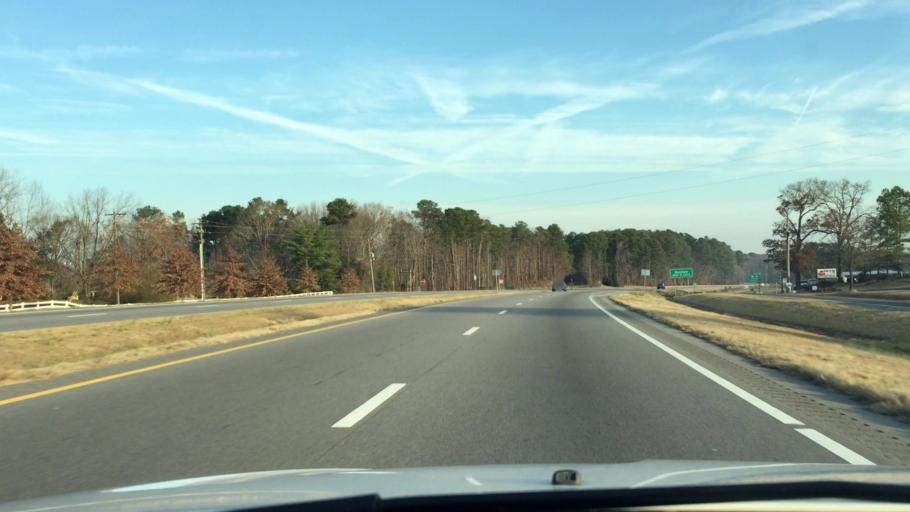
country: US
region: North Carolina
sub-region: Lee County
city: Sanford
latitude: 35.4493
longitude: -79.2147
